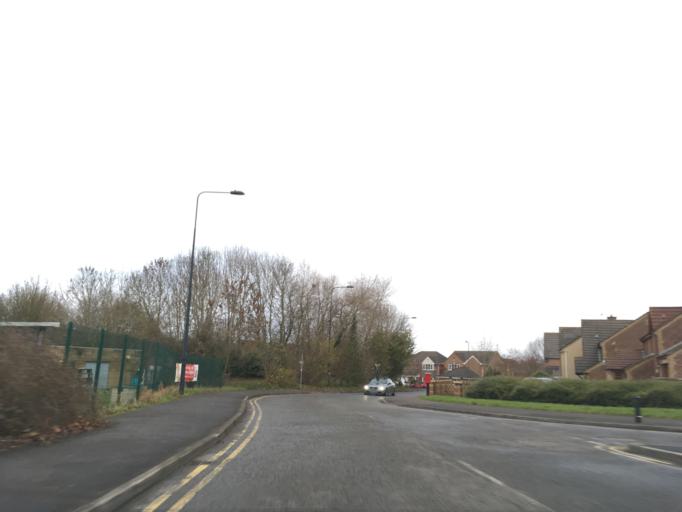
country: GB
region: England
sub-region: South Gloucestershire
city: Stoke Gifford
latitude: 51.5186
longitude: -2.5333
